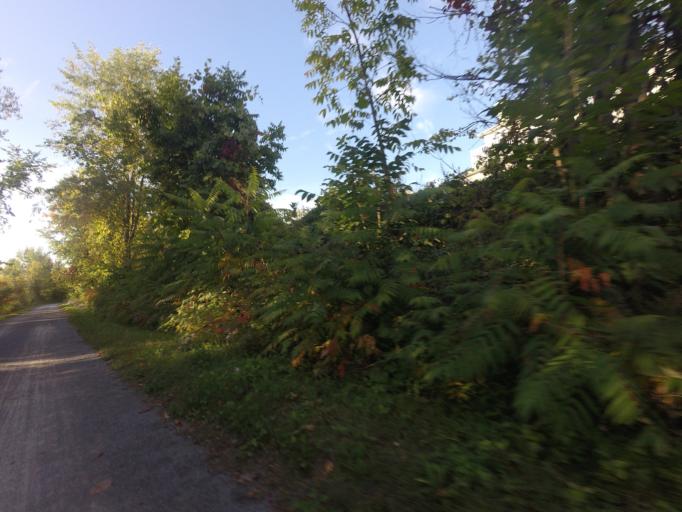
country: CA
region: Quebec
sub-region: Laurentides
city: Prevost
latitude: 45.8482
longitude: -74.0635
